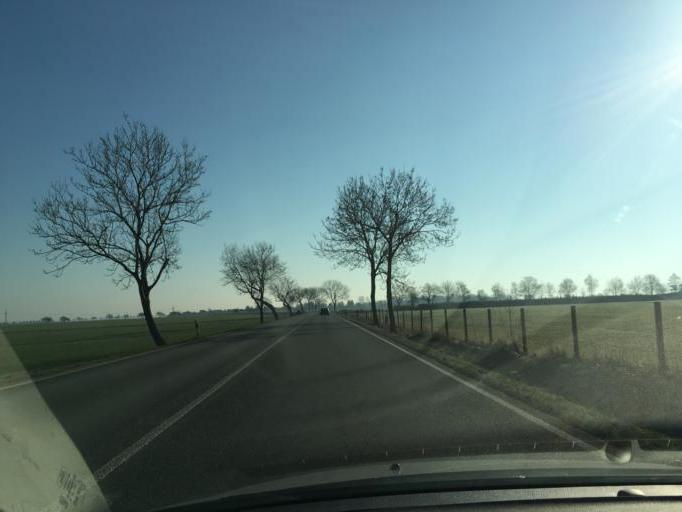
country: DE
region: Saxony
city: Grossposna
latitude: 51.2621
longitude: 12.5110
